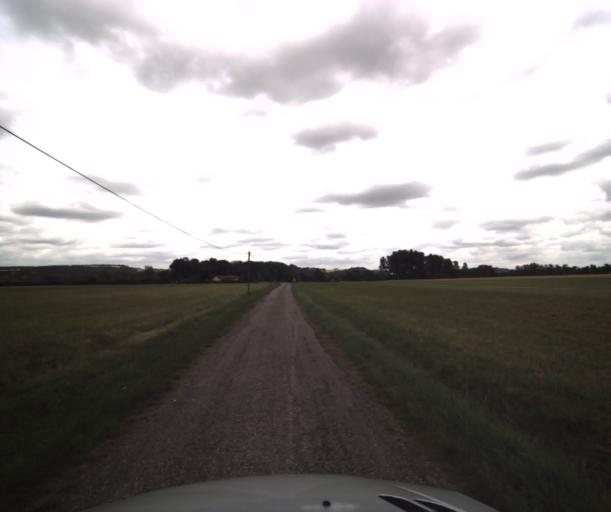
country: FR
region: Midi-Pyrenees
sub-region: Departement de la Haute-Garonne
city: Labarthe-sur-Leze
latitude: 43.4669
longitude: 1.4029
